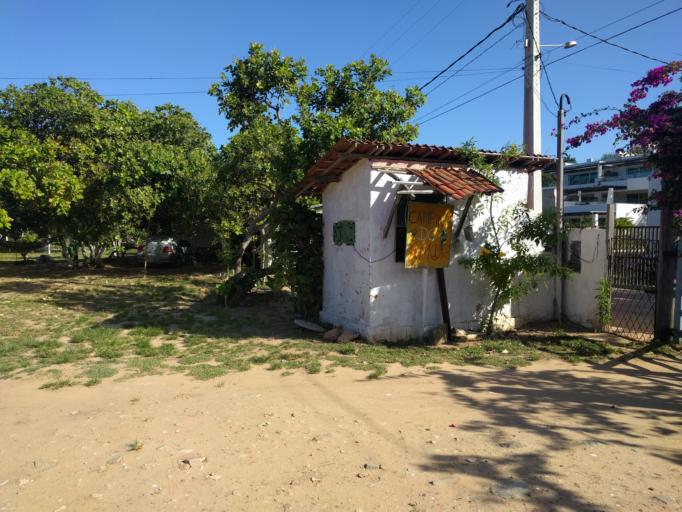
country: BR
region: Rio Grande do Norte
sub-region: Ares
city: Ares
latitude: -6.2322
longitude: -35.0427
